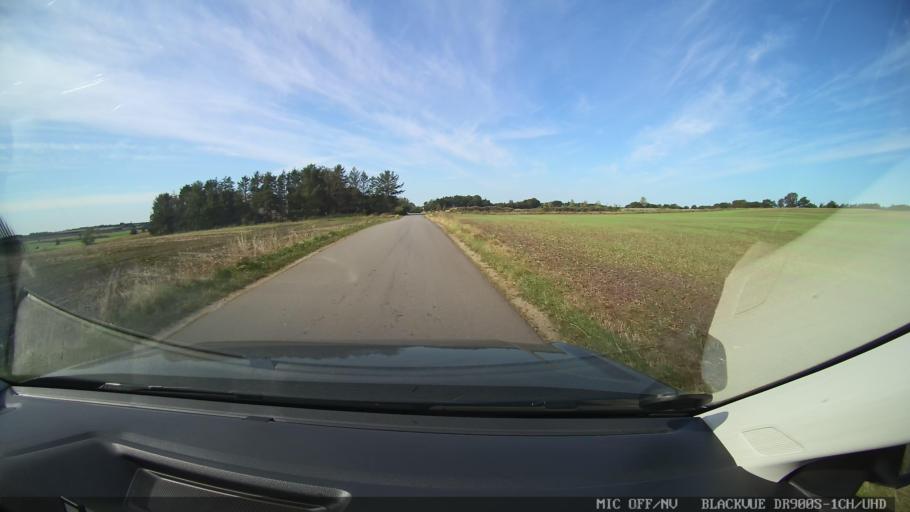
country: DK
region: North Denmark
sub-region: Mariagerfjord Kommune
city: Hobro
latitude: 56.5353
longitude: 9.7590
